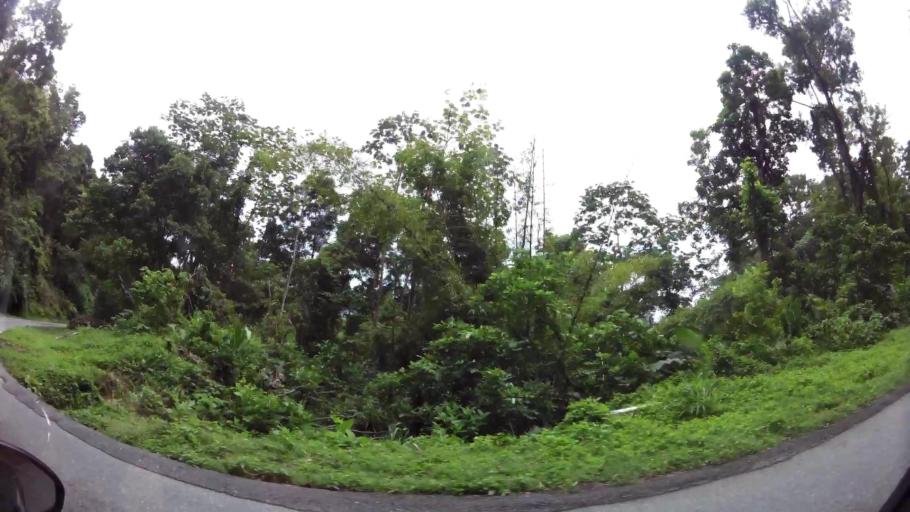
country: TT
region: Diego Martin
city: Petit Valley
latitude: 10.7443
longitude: -61.4943
